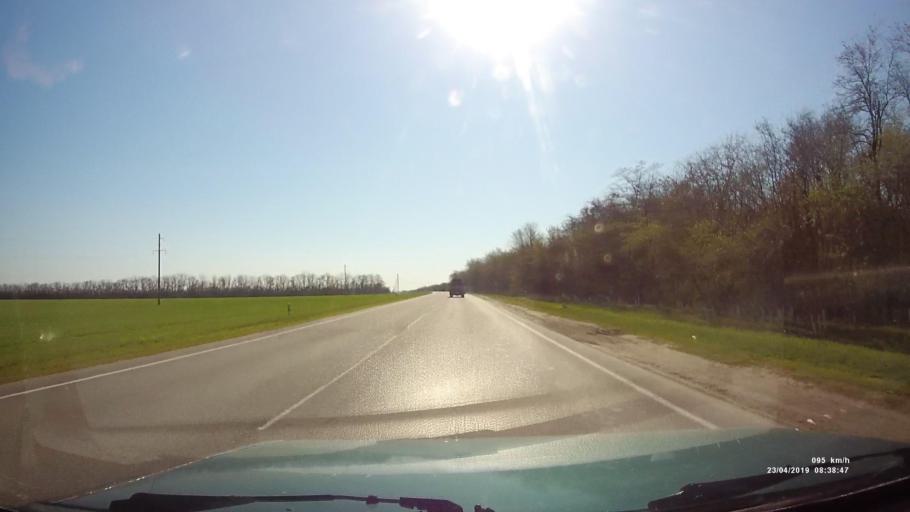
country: RU
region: Rostov
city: Gigant
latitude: 46.5291
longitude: 41.1944
